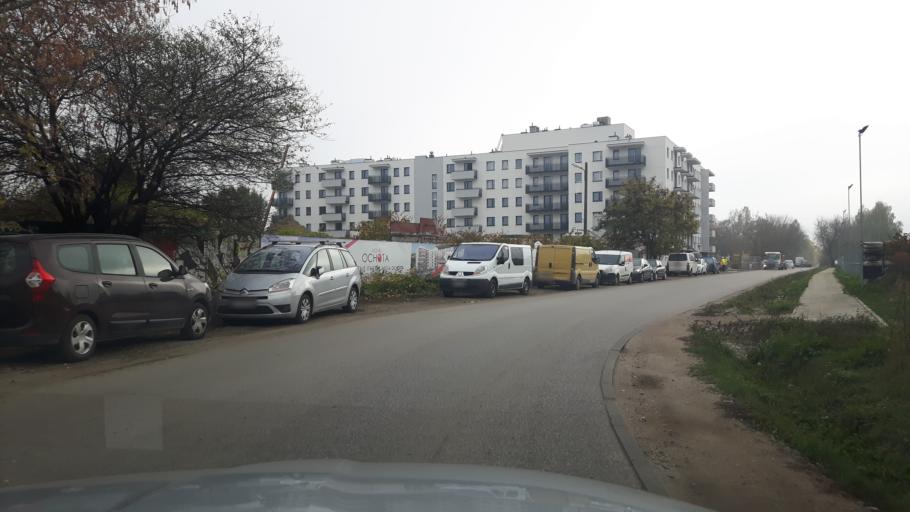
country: PL
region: Masovian Voivodeship
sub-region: Warszawa
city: Wlochy
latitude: 52.2021
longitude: 20.9444
